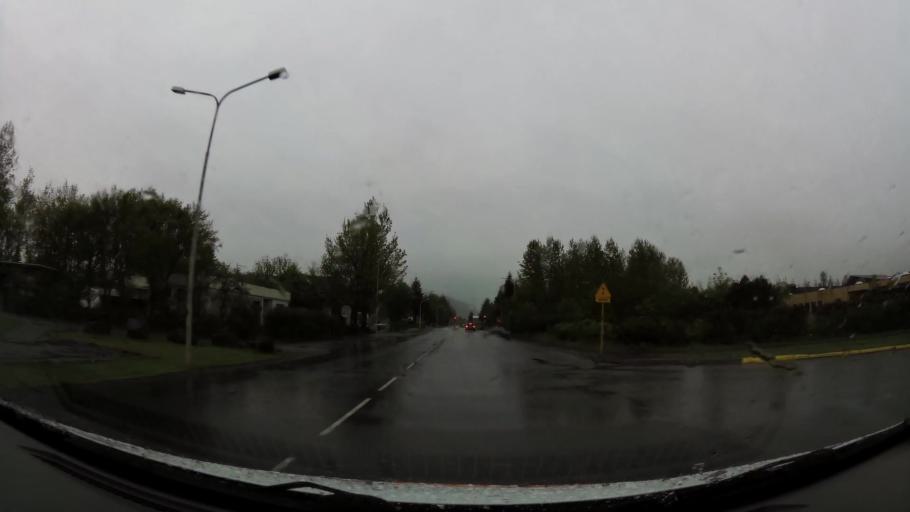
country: IS
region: South
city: Selfoss
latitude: 63.9330
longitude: -20.9991
